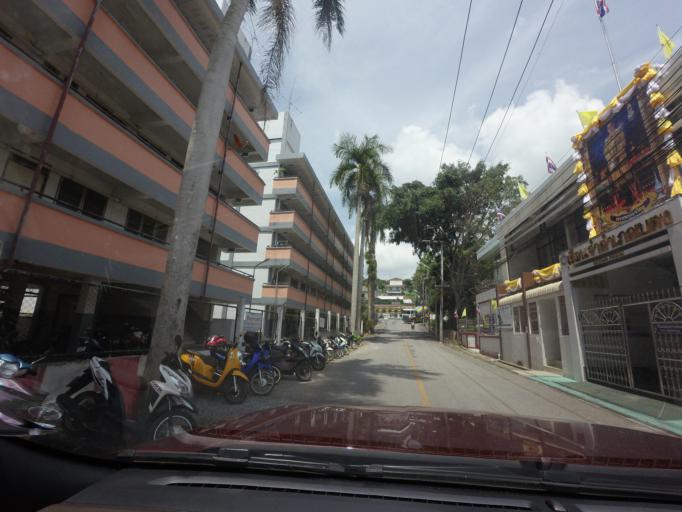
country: TH
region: Yala
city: Betong
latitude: 5.7729
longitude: 101.0671
